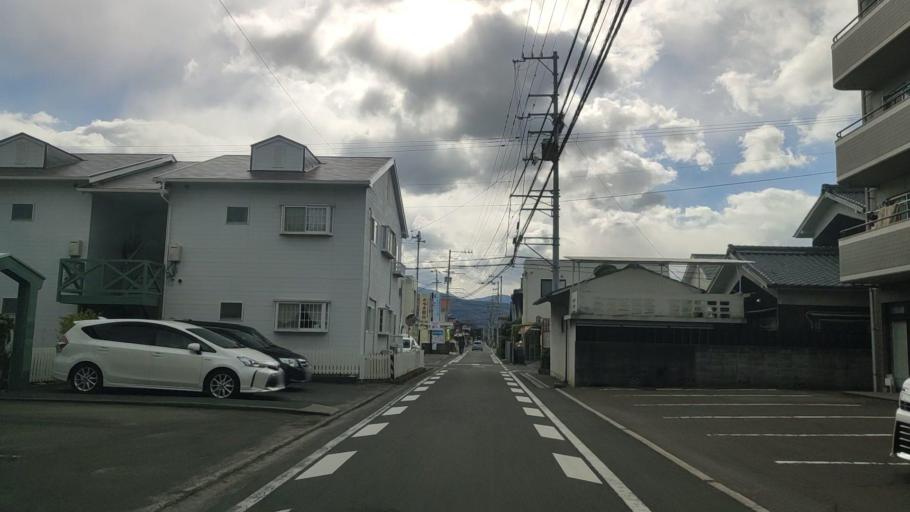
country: JP
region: Ehime
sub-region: Shikoku-chuo Shi
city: Matsuyama
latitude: 33.8124
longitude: 132.7525
